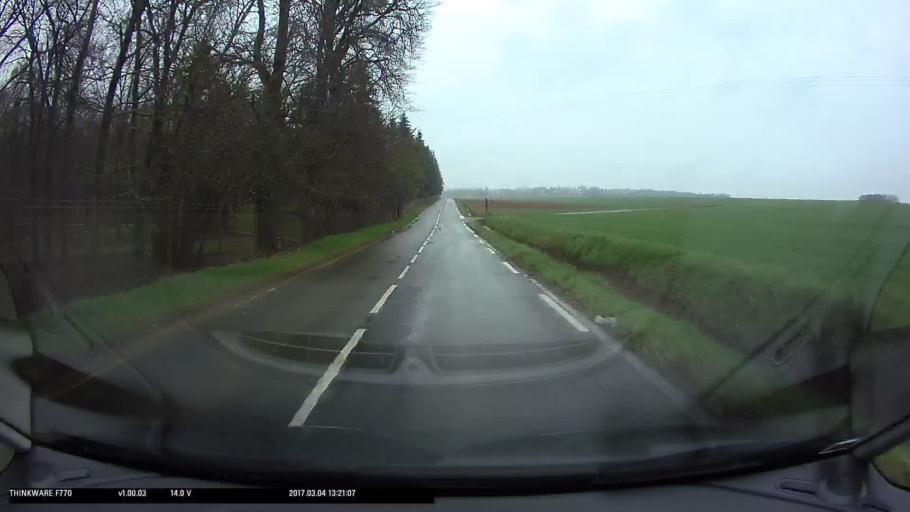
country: FR
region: Ile-de-France
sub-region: Departement du Val-d'Oise
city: Us
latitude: 49.1102
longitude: 1.9769
